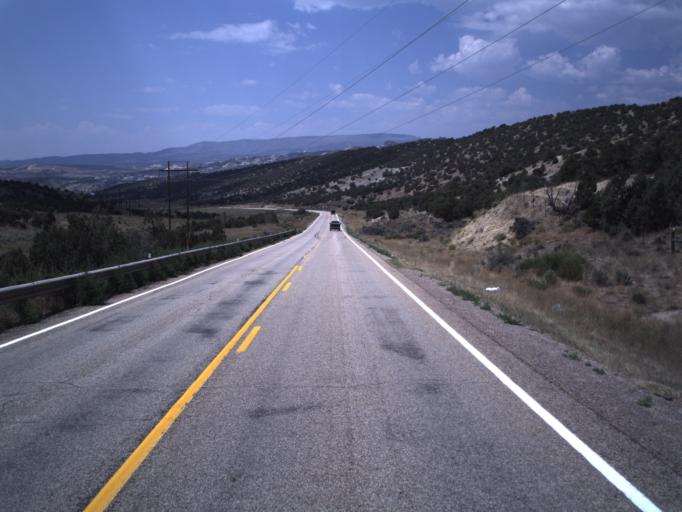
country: US
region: Utah
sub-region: Uintah County
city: Vernal
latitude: 40.5733
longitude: -109.4841
